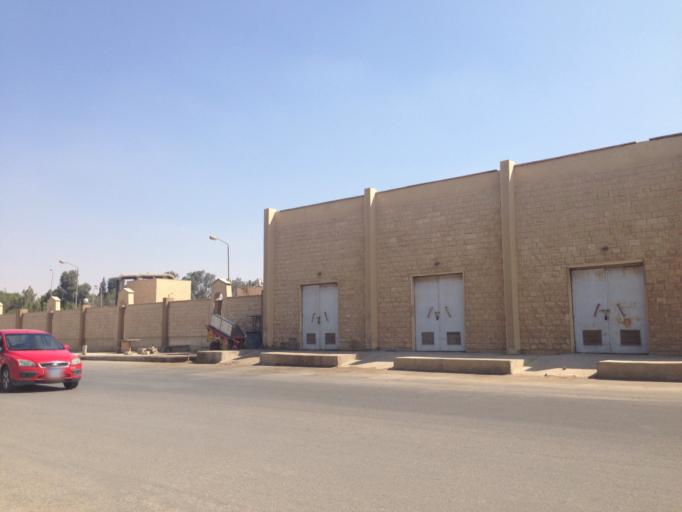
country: EG
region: Muhafazat al Qalyubiyah
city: Al Khankah
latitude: 30.0666
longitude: 31.4259
